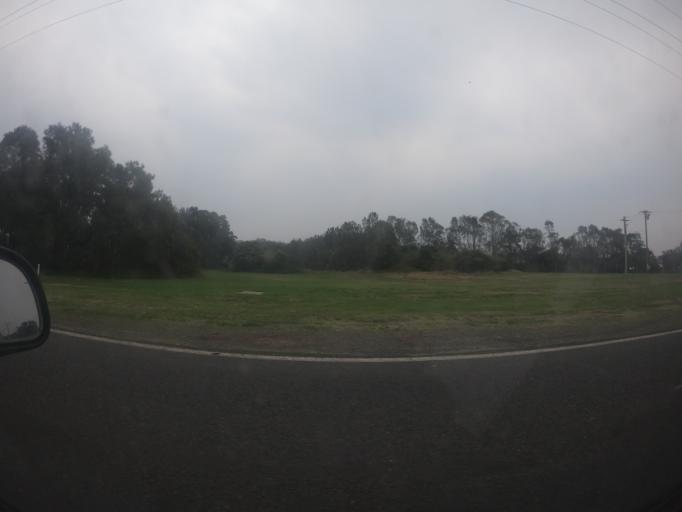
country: AU
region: New South Wales
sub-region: Shellharbour
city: Barrack Heights
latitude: -34.5708
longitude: 150.8664
